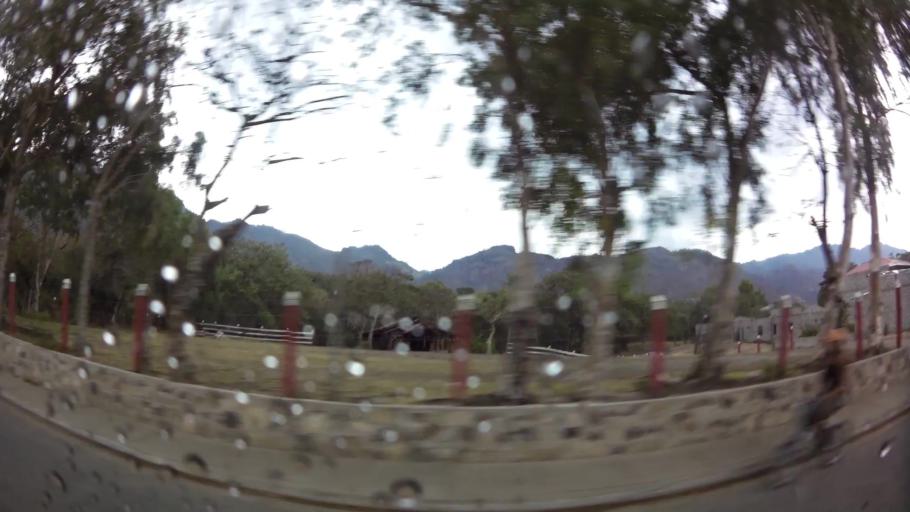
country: NI
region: Jinotega
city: Jinotega
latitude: 13.1025
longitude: -86.0040
